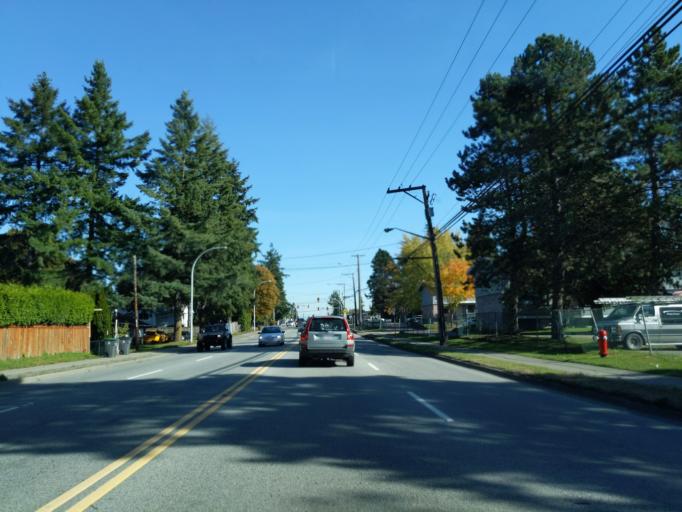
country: CA
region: British Columbia
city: Port Moody
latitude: 49.1987
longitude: -122.8203
